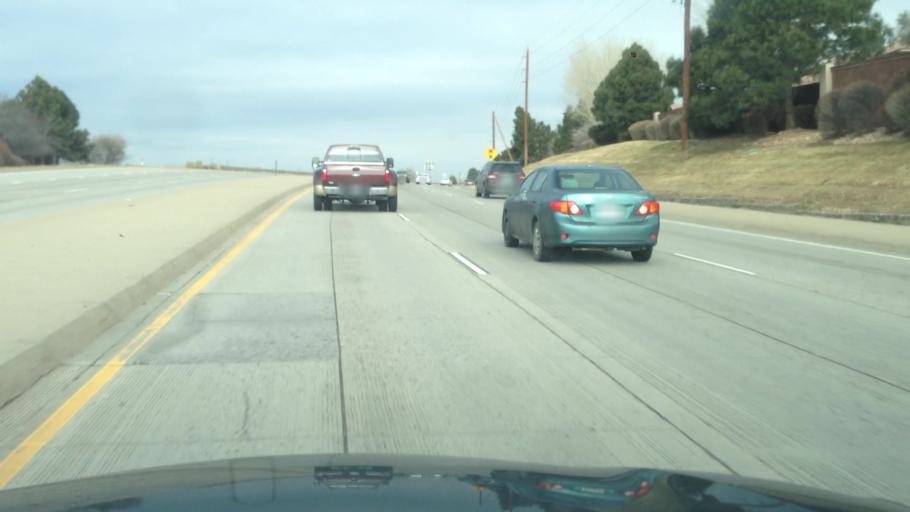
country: US
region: Colorado
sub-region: Arapahoe County
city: Dove Valley
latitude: 39.6339
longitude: -104.8279
